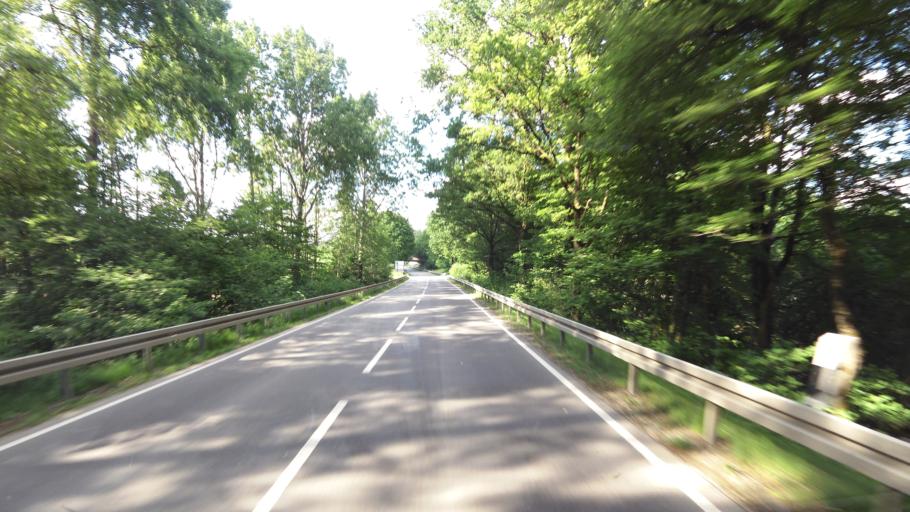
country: DE
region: Bavaria
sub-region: Upper Bavaria
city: Hohenpolding
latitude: 48.3806
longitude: 12.1277
